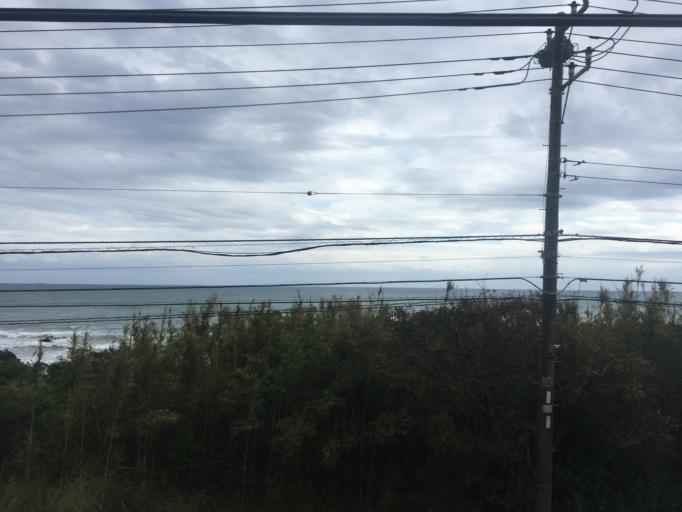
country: JP
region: Chiba
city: Kawaguchi
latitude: 35.0323
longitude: 140.0037
